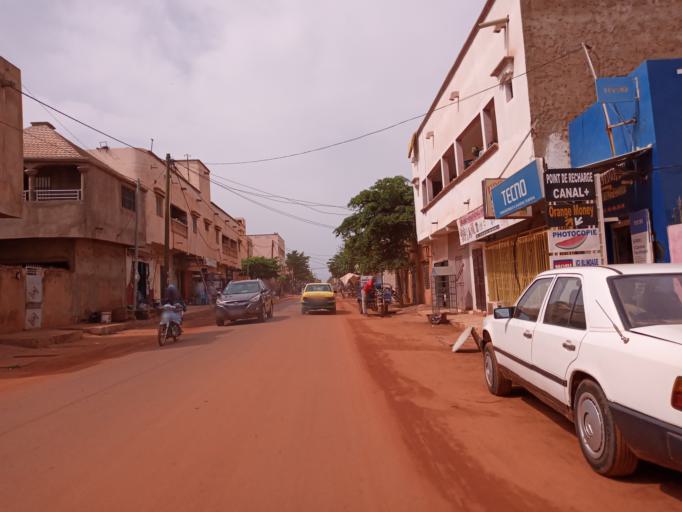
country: ML
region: Bamako
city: Bamako
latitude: 12.5575
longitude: -7.9903
